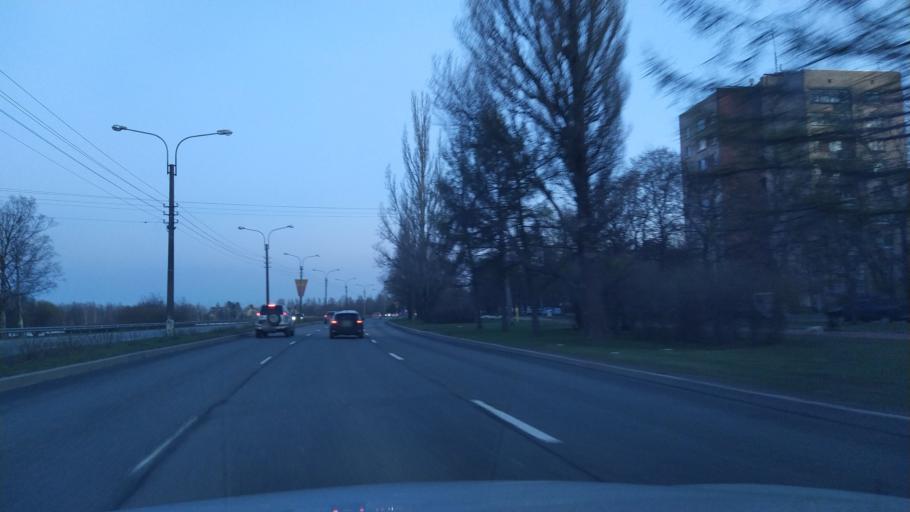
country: RU
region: St.-Petersburg
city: Sestroretsk
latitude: 60.0990
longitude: 29.9803
